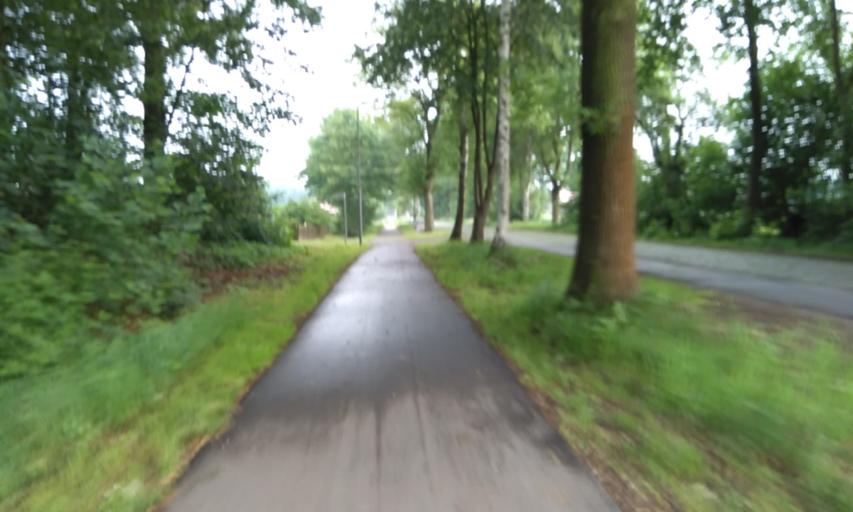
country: DE
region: Lower Saxony
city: Deinste
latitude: 53.5167
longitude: 9.4465
